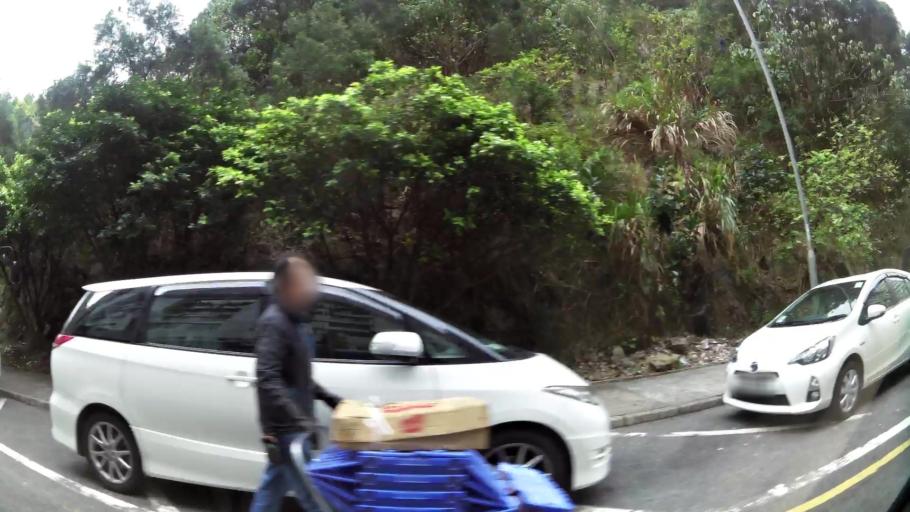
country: HK
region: Sha Tin
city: Sha Tin
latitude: 22.4002
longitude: 114.1932
